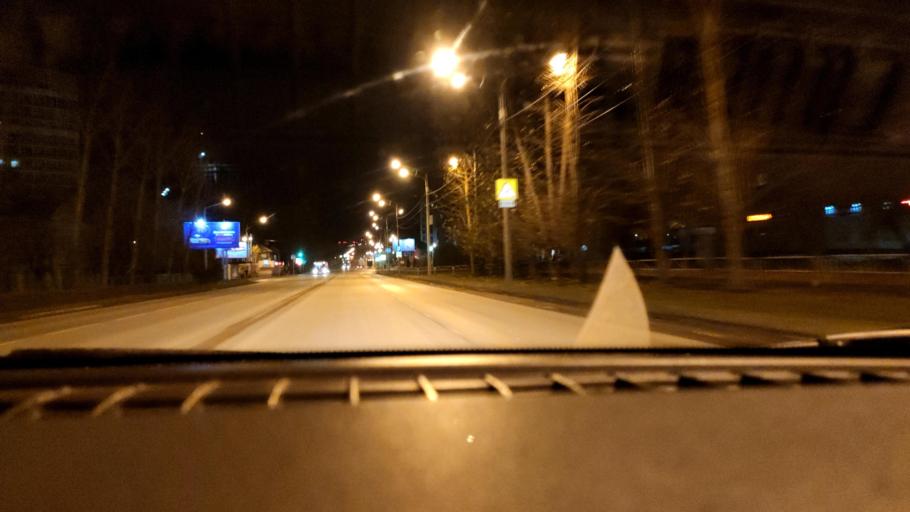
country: RU
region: Perm
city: Perm
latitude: 57.9789
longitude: 56.2157
